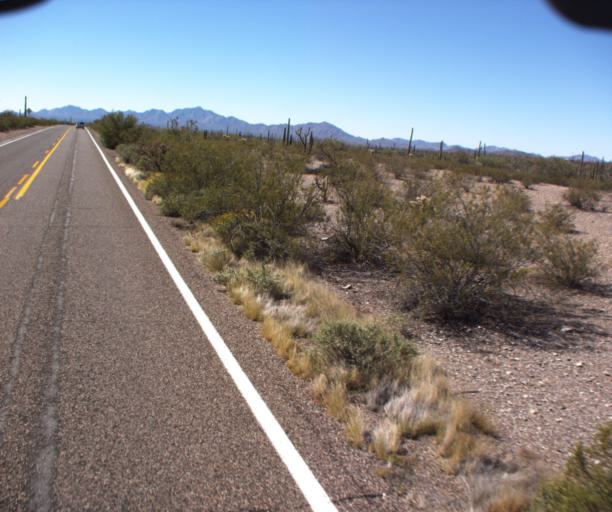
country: MX
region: Sonora
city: Sonoyta
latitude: 31.9424
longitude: -112.7989
